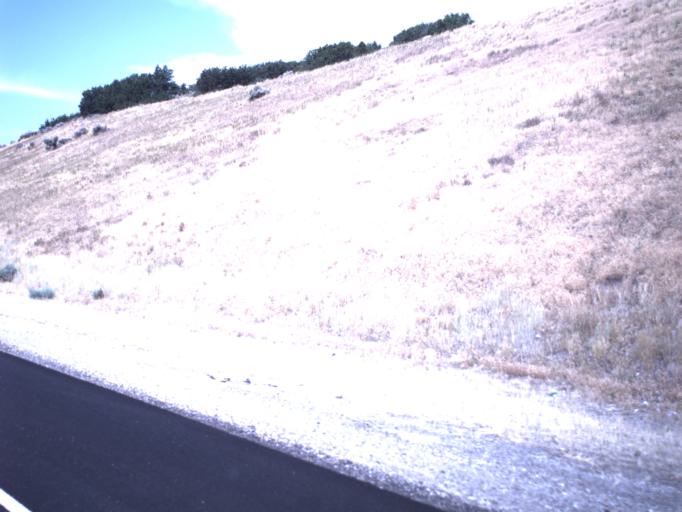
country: US
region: Utah
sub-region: Summit County
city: Kamas
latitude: 40.6362
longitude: -111.3384
